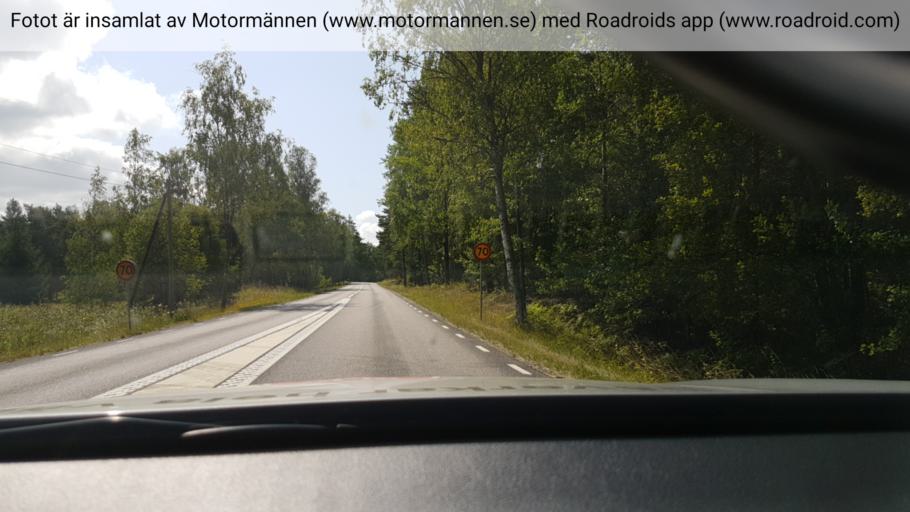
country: SE
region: Stockholm
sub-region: Osterakers Kommun
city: Akersberga
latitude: 59.5567
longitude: 18.2201
